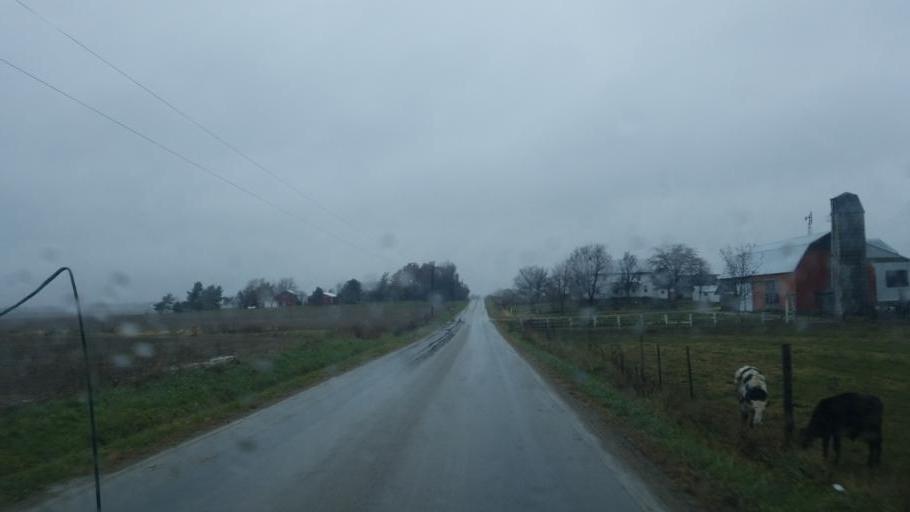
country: US
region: Indiana
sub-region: Adams County
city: Geneva
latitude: 40.6228
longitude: -84.9356
